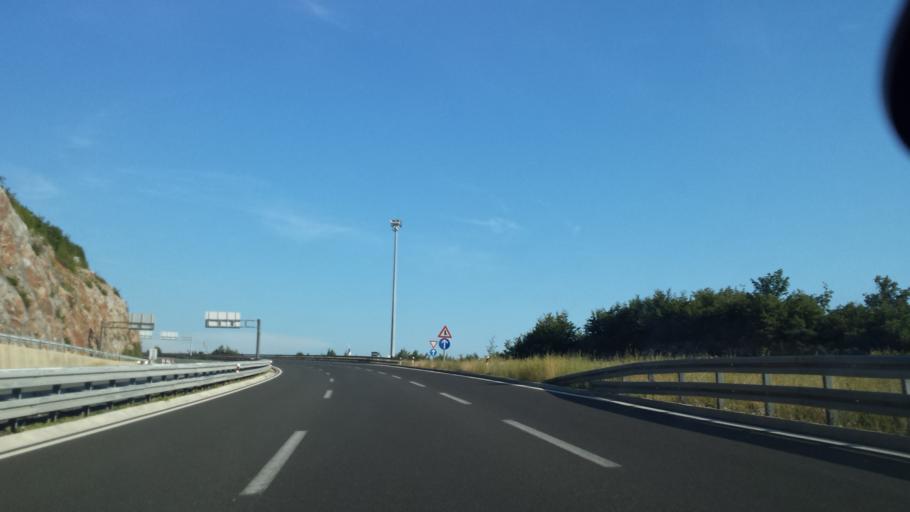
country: HR
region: Primorsko-Goranska
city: Krasica
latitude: 45.3338
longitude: 14.5968
